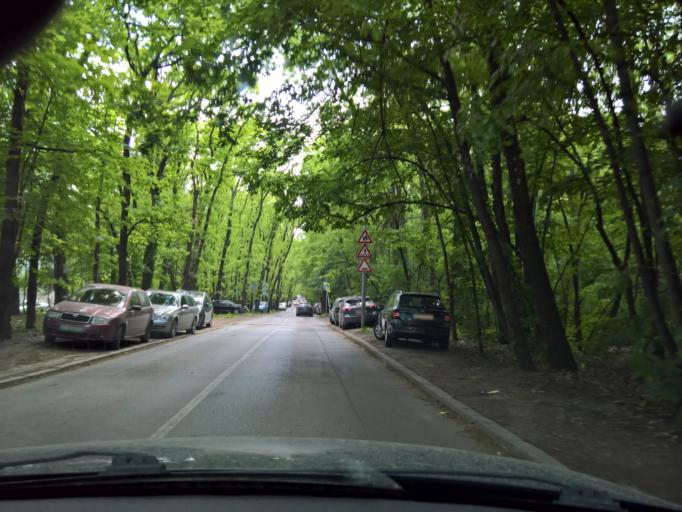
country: BG
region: Sofia-Capital
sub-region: Stolichna Obshtina
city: Sofia
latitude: 42.6773
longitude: 23.3529
